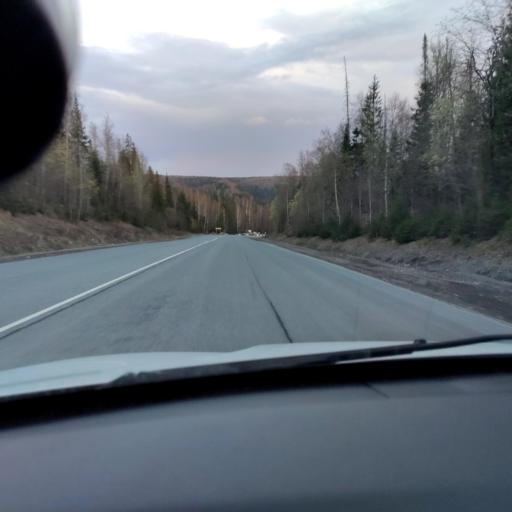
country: RU
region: Perm
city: Gremyachinsk
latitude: 58.4487
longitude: 57.8723
